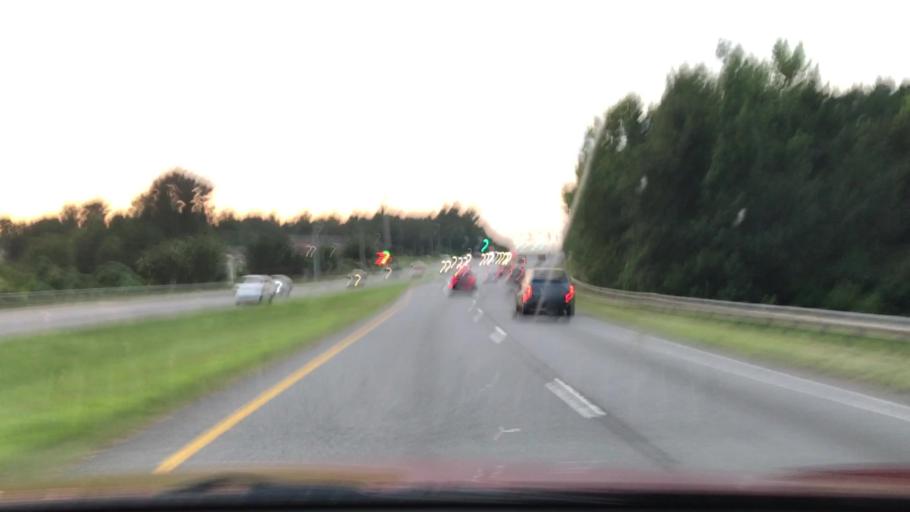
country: US
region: Georgia
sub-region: Gwinnett County
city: Sugar Hill
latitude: 34.0426
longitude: -83.9916
